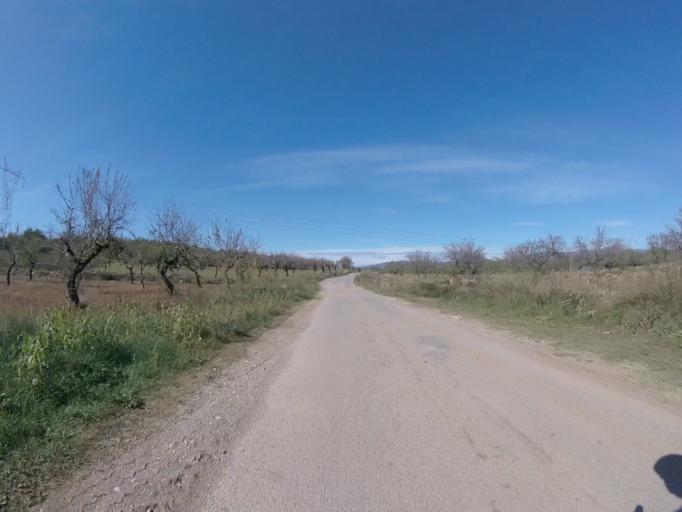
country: ES
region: Valencia
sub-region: Provincia de Castello
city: Benlloch
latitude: 40.2099
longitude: 0.0404
